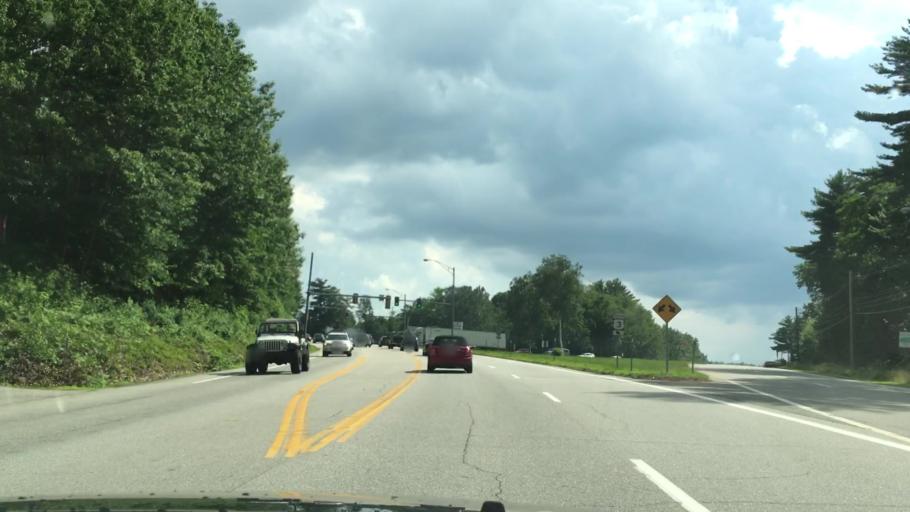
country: US
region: New Hampshire
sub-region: Belknap County
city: Meredith
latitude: 43.6469
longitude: -71.5008
